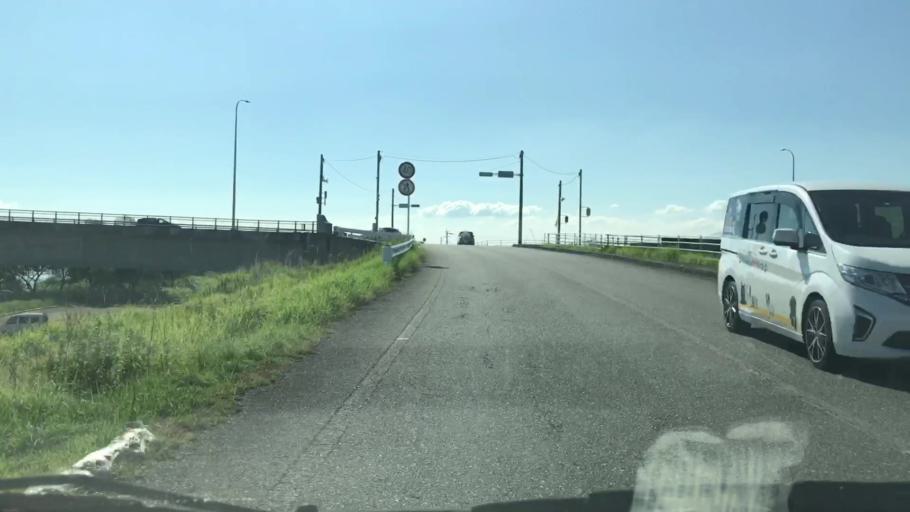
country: JP
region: Saga Prefecture
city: Kanzakimachi-kanzaki
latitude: 33.2726
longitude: 130.4318
